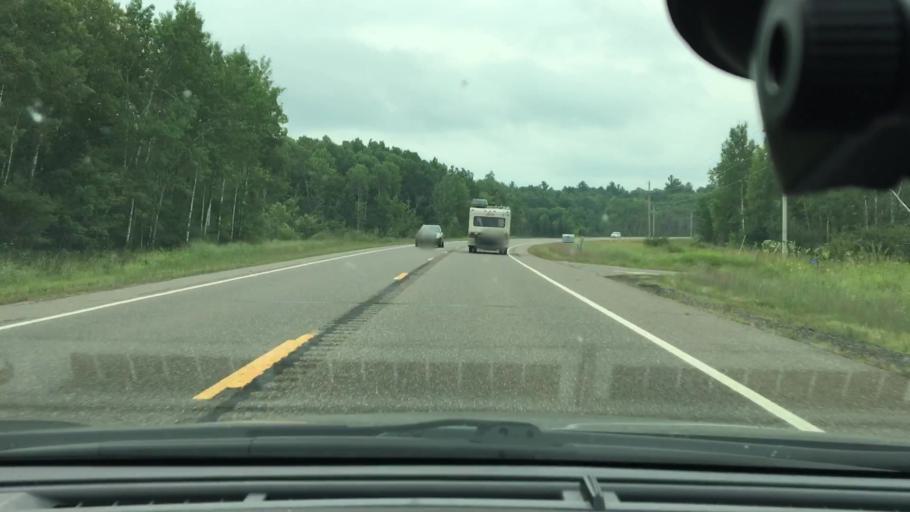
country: US
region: Minnesota
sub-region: Crow Wing County
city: Crosby
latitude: 46.5056
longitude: -93.9583
